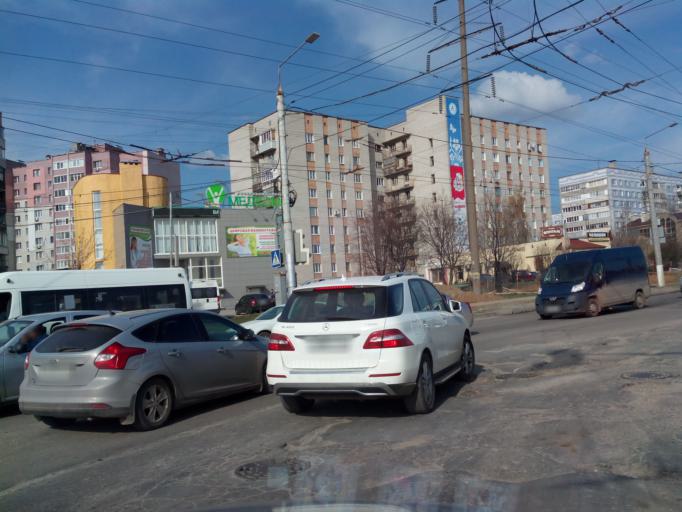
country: RU
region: Rjazan
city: Ryazan'
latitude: 54.6601
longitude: 39.6638
